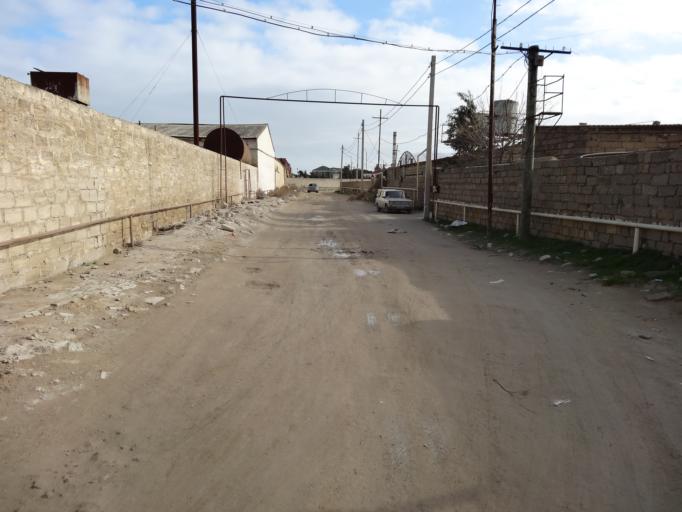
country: AZ
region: Baki
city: Mardakyany
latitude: 40.5025
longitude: 50.1955
